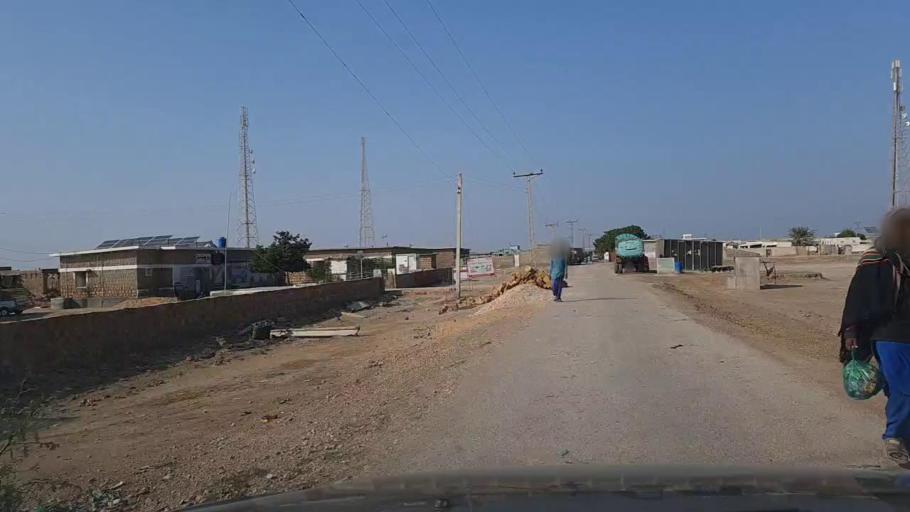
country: PK
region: Sindh
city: Keti Bandar
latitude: 24.1415
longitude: 67.4513
